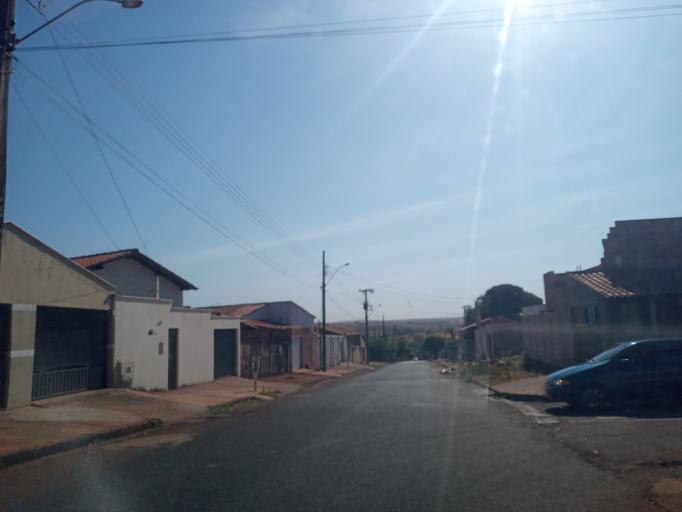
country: BR
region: Minas Gerais
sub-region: Ituiutaba
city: Ituiutaba
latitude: -18.9548
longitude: -49.4600
